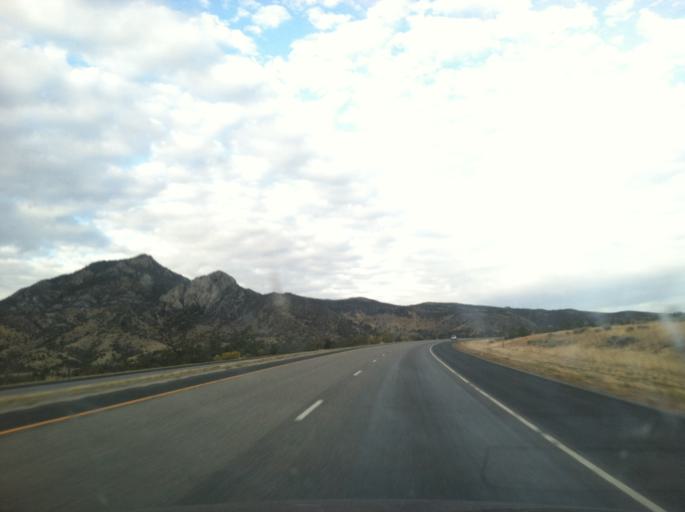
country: US
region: Montana
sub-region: Jefferson County
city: Whitehall
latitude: 45.8819
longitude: -111.9163
